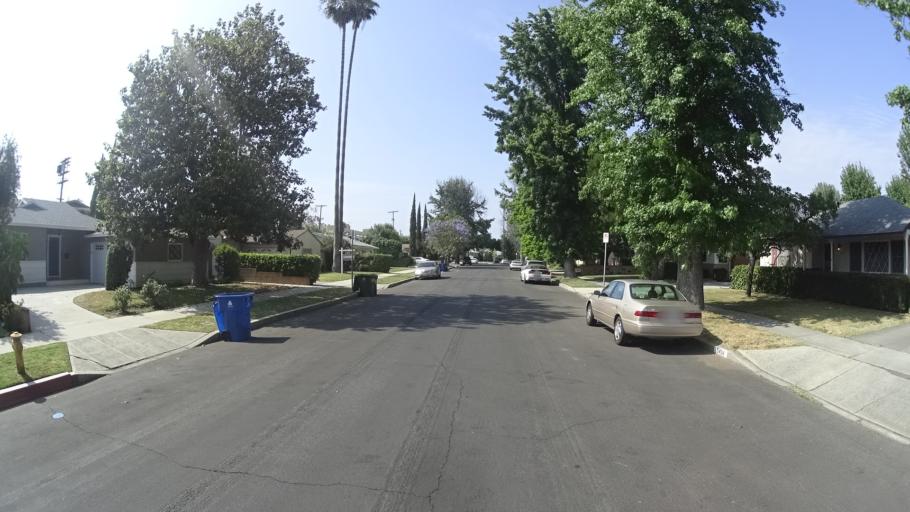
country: US
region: California
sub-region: Los Angeles County
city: Van Nuys
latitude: 34.1695
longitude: -118.4648
